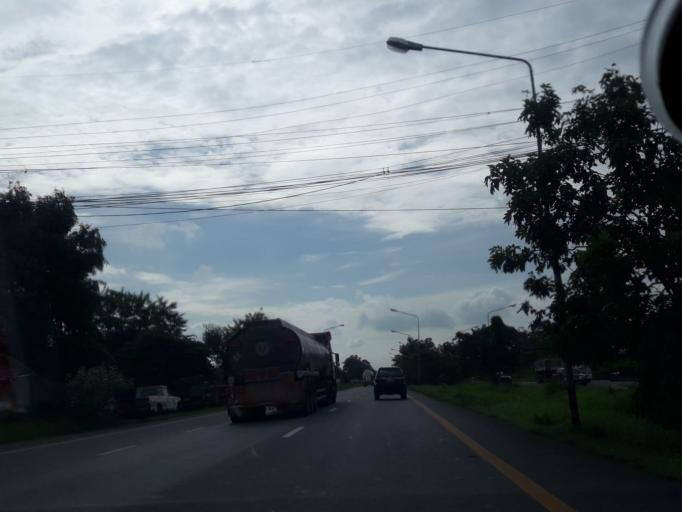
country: TH
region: Sara Buri
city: Saraburi
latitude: 14.5510
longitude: 100.9363
